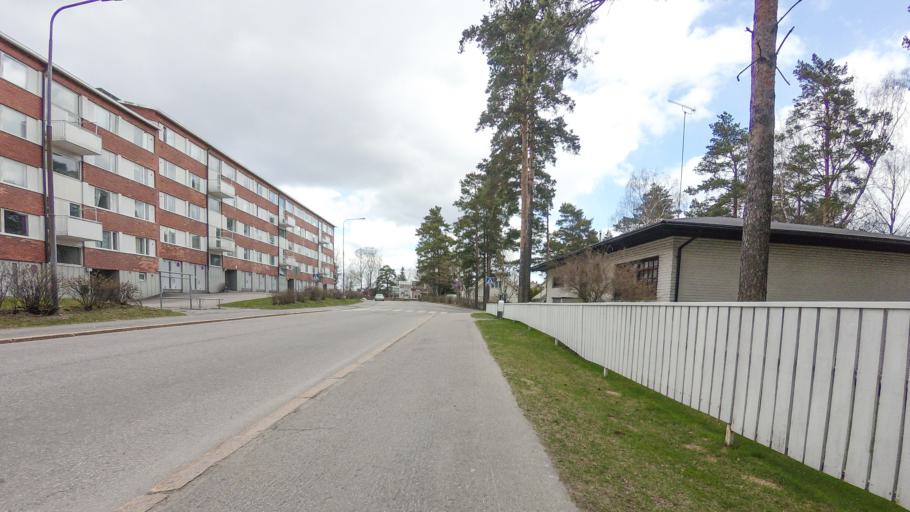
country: FI
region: Uusimaa
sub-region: Helsinki
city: Vantaa
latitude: 60.2155
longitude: 25.1051
